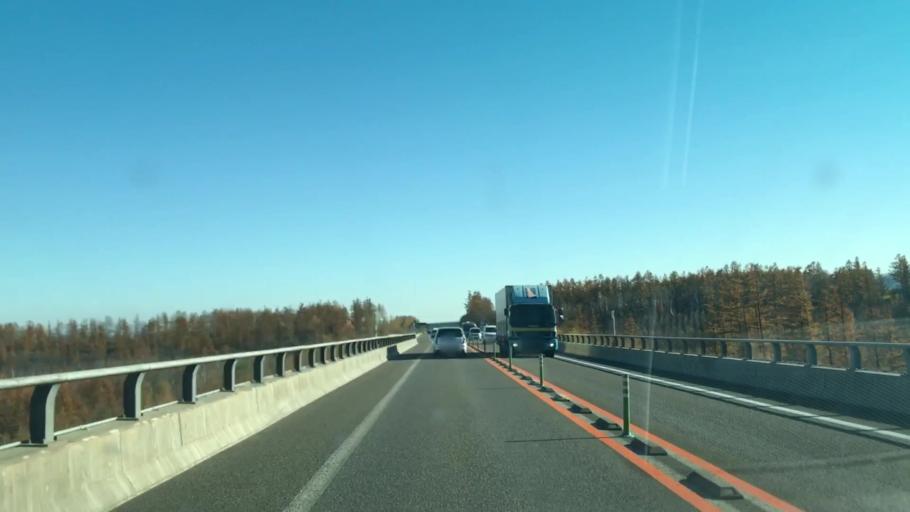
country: JP
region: Hokkaido
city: Otofuke
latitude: 43.0028
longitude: 142.8471
